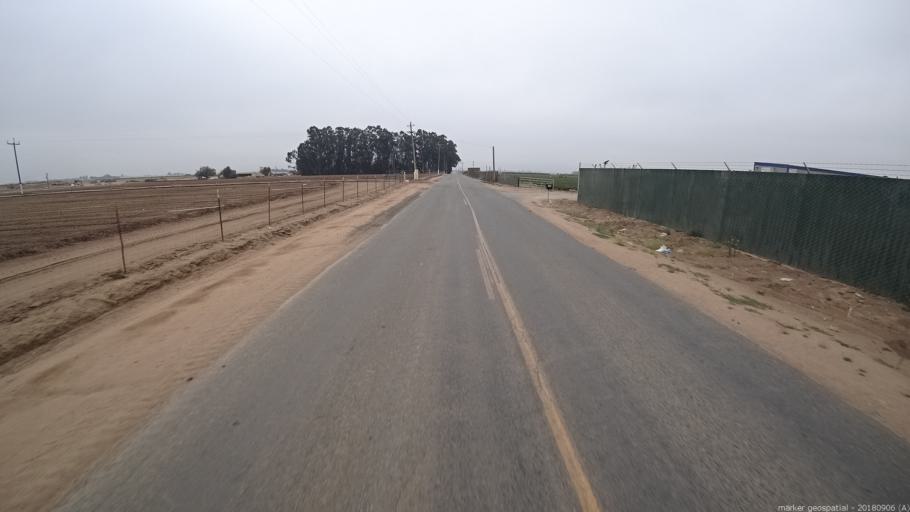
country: US
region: California
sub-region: Monterey County
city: Chualar
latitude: 36.6547
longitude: -121.5590
